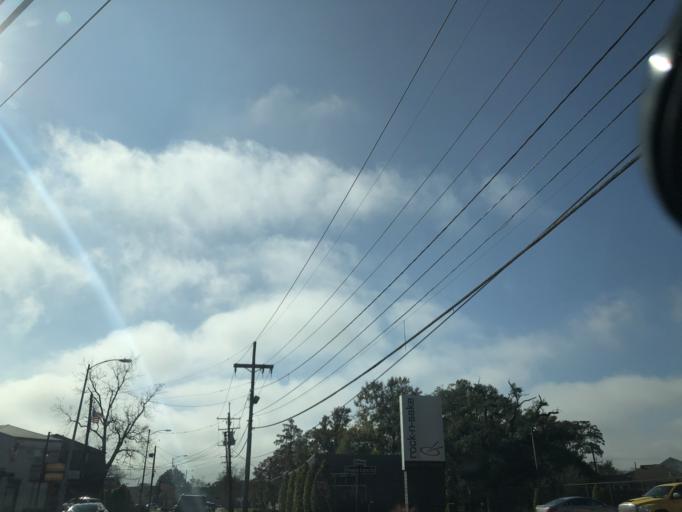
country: US
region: Louisiana
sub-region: Jefferson Parish
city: Metairie
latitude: 29.9791
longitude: -90.1528
